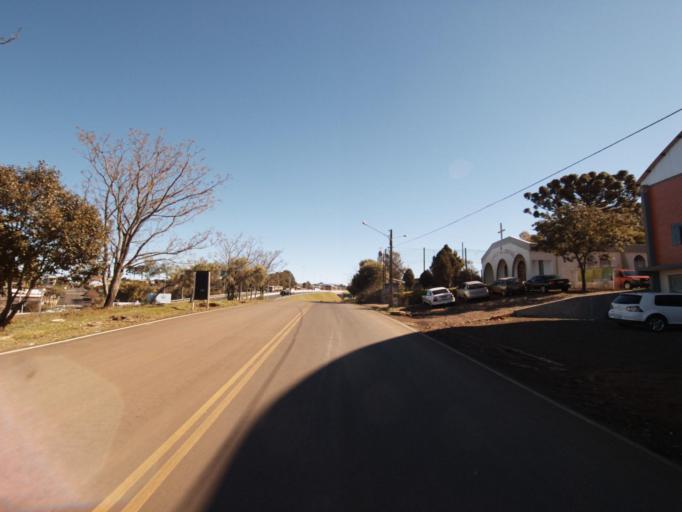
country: BR
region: Santa Catarina
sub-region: Xanxere
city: Xanxere
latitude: -26.8847
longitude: -52.4115
